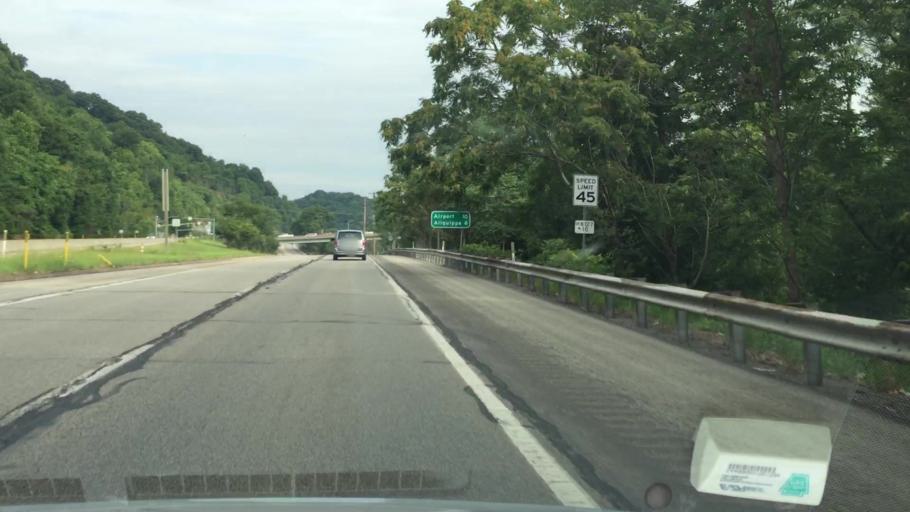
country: US
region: Pennsylvania
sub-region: Allegheny County
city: Sewickley
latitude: 40.5290
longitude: -80.1870
